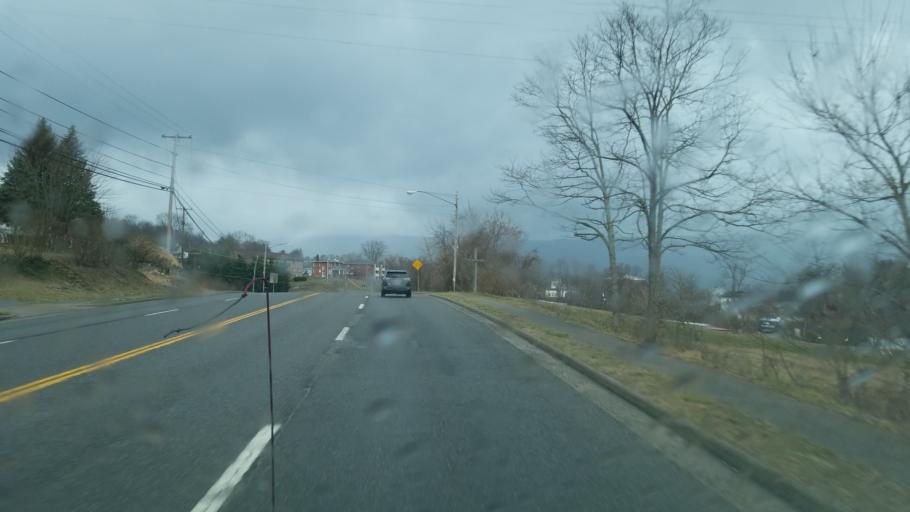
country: US
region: Virginia
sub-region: Giles County
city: Pearisburg
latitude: 37.3228
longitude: -80.7320
